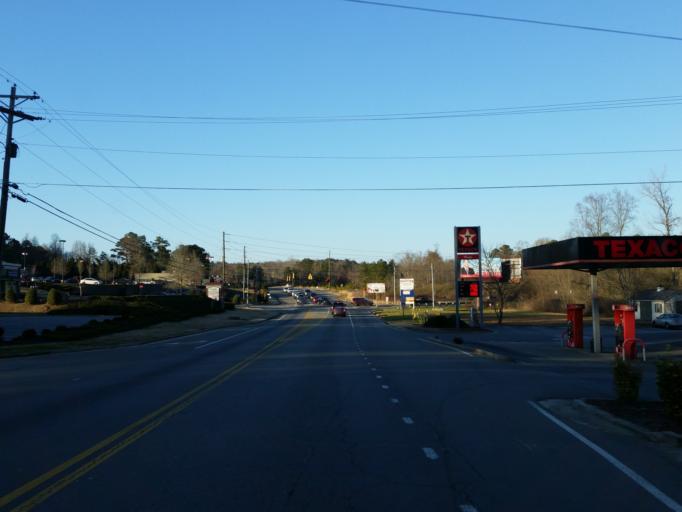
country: US
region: Georgia
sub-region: Cherokee County
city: Woodstock
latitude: 34.1282
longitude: -84.4982
